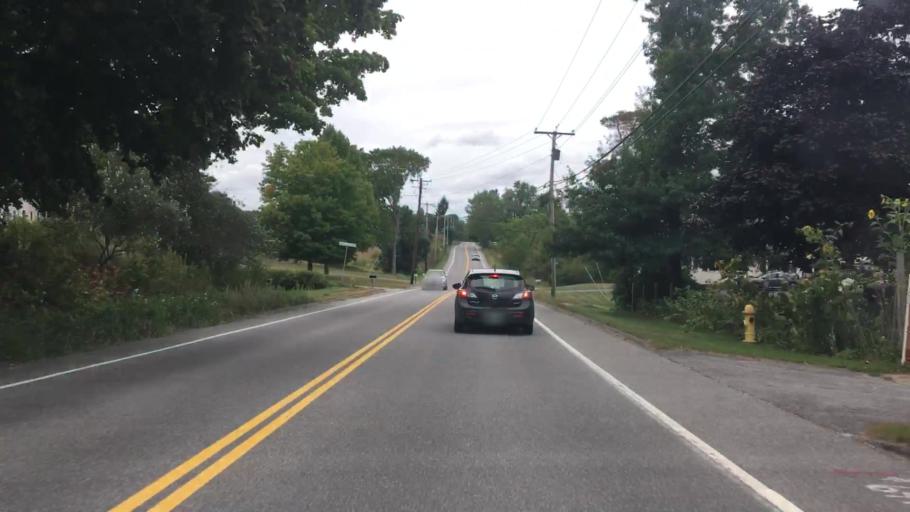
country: US
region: Maine
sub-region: Cumberland County
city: Yarmouth
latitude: 43.8247
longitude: -70.1919
